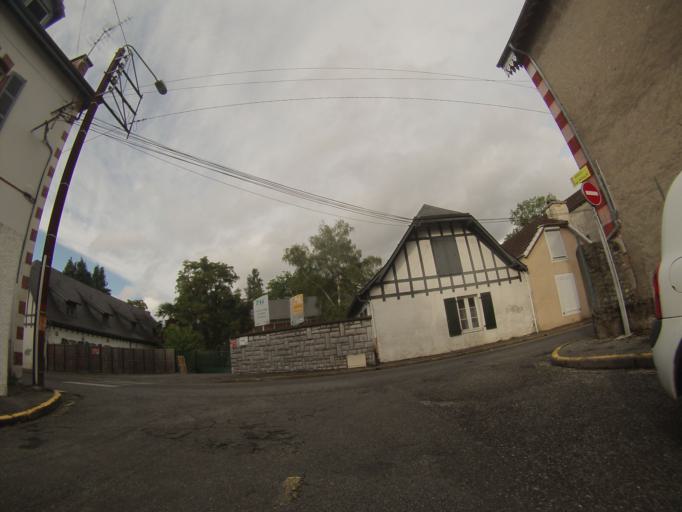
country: FR
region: Aquitaine
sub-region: Departement des Pyrenees-Atlantiques
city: Gelos
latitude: 43.2837
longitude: -0.3739
